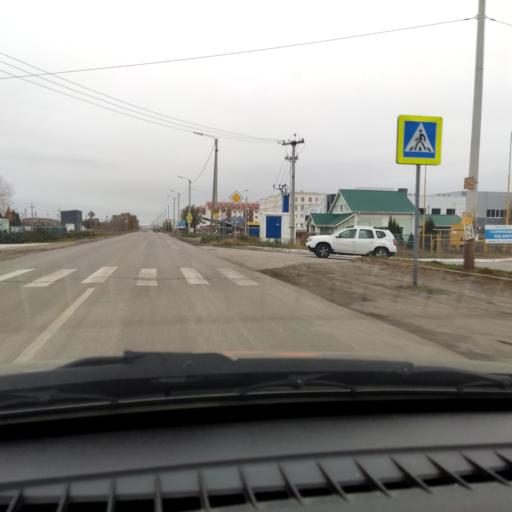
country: RU
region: Samara
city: Podstepki
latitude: 53.5216
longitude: 49.1943
